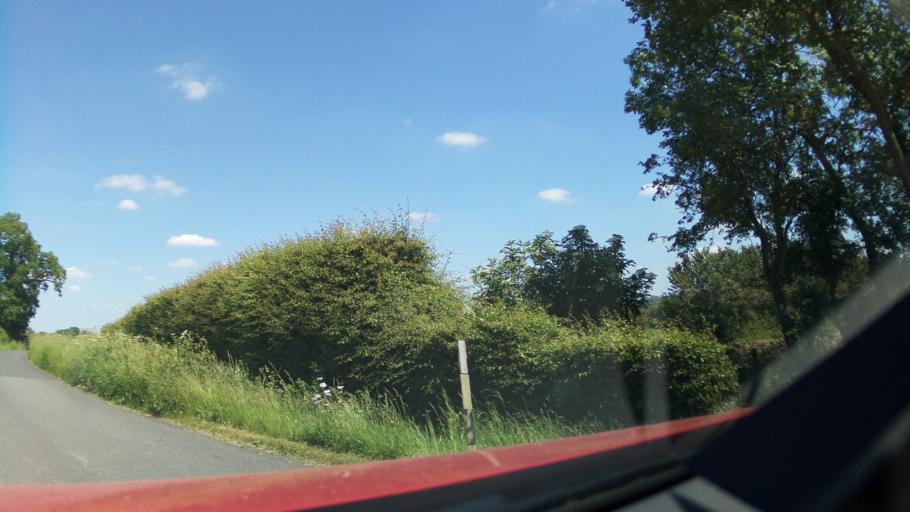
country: GB
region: England
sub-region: Wiltshire
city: Royal Wootton Bassett
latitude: 51.5125
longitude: -1.8961
